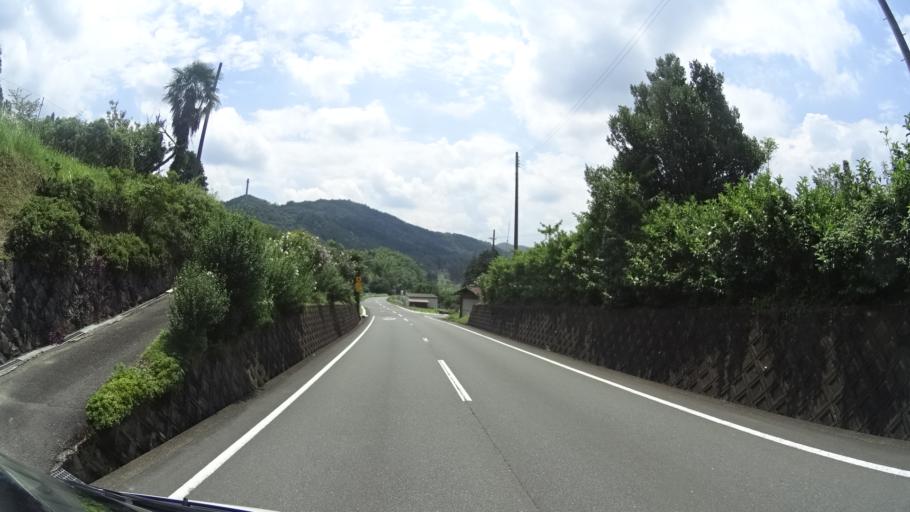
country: JP
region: Kyoto
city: Ayabe
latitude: 35.1984
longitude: 135.2626
